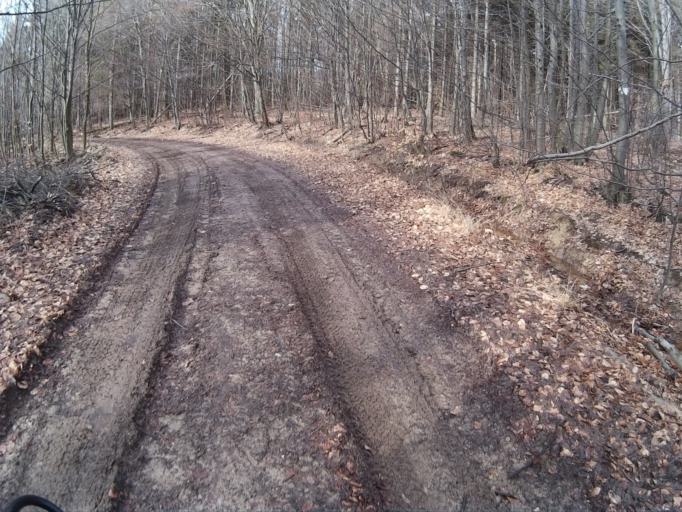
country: HU
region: Borsod-Abauj-Zemplen
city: Tolcsva
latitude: 48.4018
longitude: 21.4544
